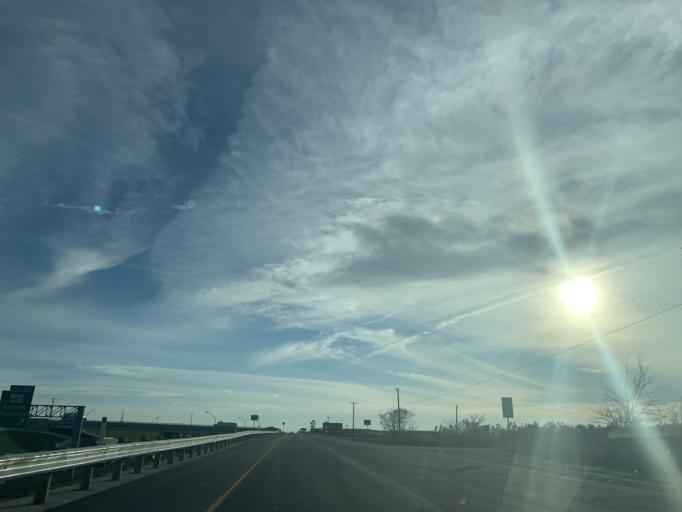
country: US
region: Texas
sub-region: Bell County
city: Salado
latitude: 30.8464
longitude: -97.5944
